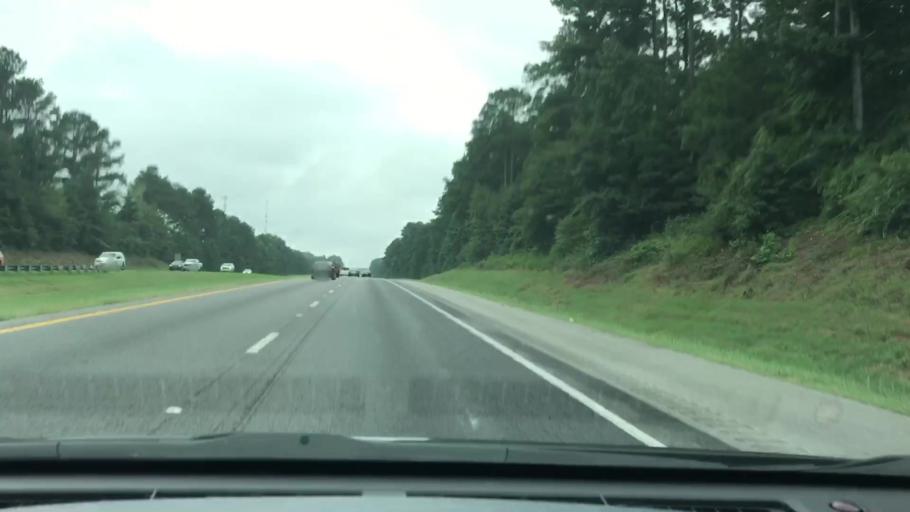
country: US
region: Georgia
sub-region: Walton County
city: Social Circle
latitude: 33.6116
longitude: -83.7206
